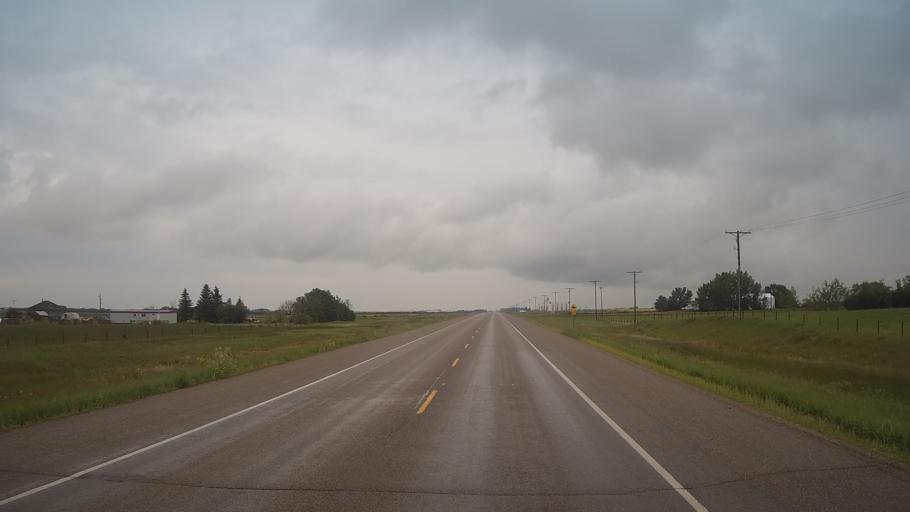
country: CA
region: Saskatchewan
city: Wilkie
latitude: 52.4057
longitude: -108.7335
